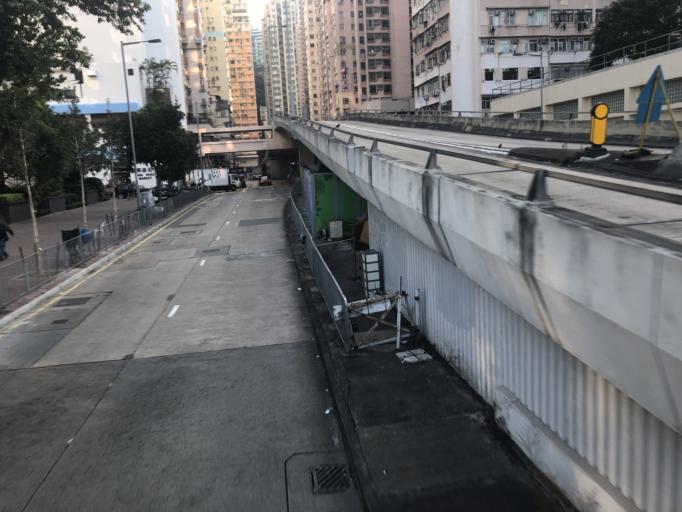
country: HK
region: Kowloon City
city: Kowloon
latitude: 22.2930
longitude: 114.1985
